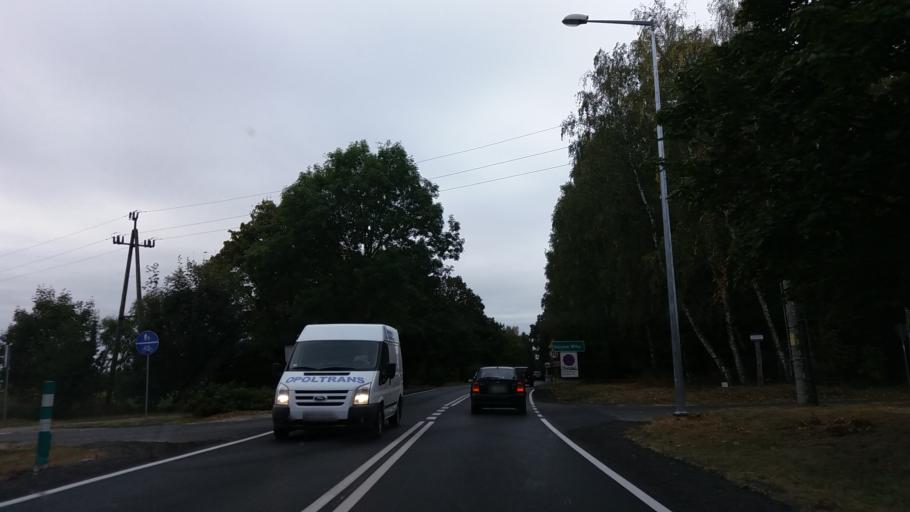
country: PL
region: Lubusz
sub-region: Powiat gorzowski
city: Klodawa
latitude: 52.7740
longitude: 15.2299
